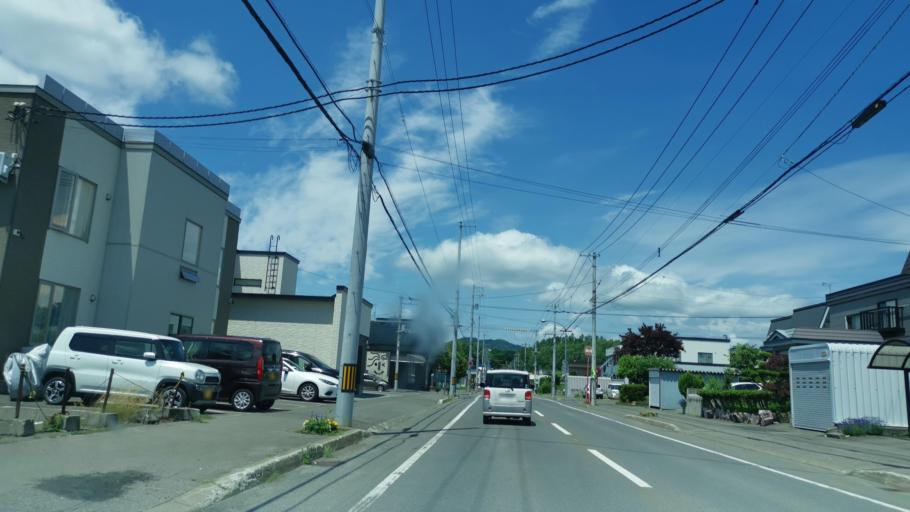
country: JP
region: Hokkaido
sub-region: Asahikawa-shi
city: Asahikawa
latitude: 43.7941
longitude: 142.3329
